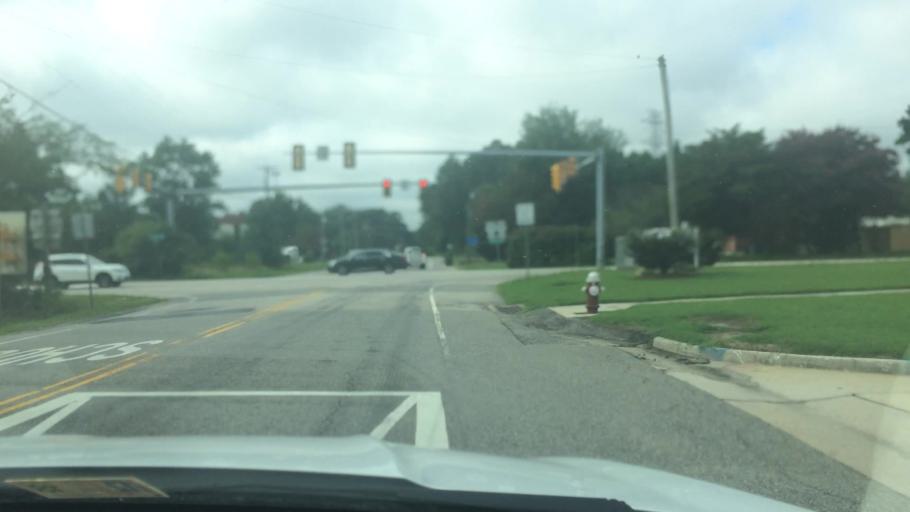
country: US
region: Virginia
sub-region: City of Poquoson
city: Poquoson
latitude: 37.1226
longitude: -76.4325
